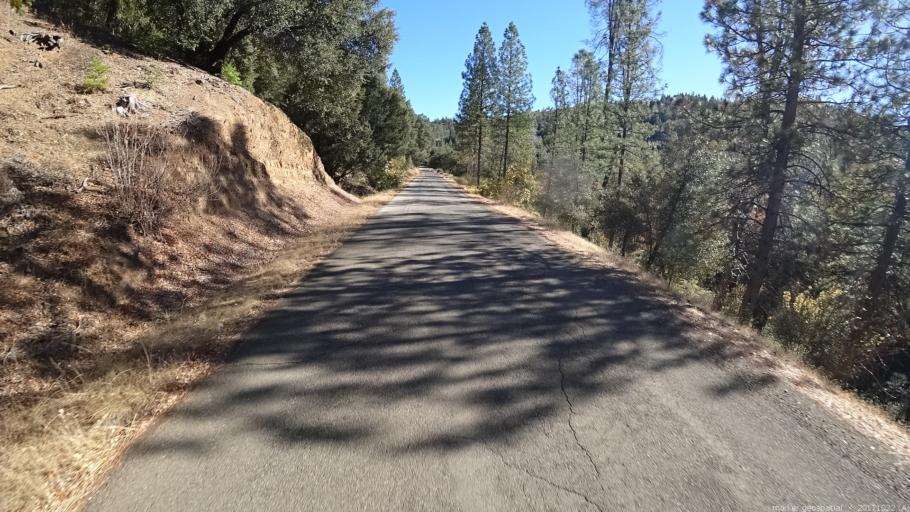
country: US
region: California
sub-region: Shasta County
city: Shasta Lake
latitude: 40.8751
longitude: -122.3643
